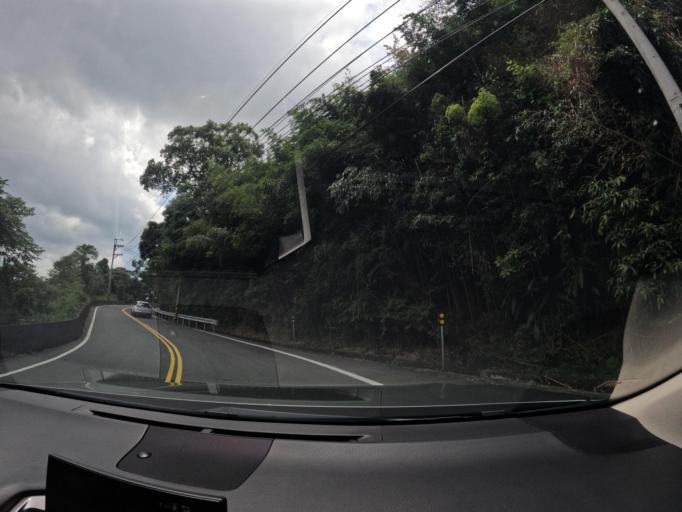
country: TW
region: Taiwan
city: Fengyuan
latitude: 24.3868
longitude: 120.8129
